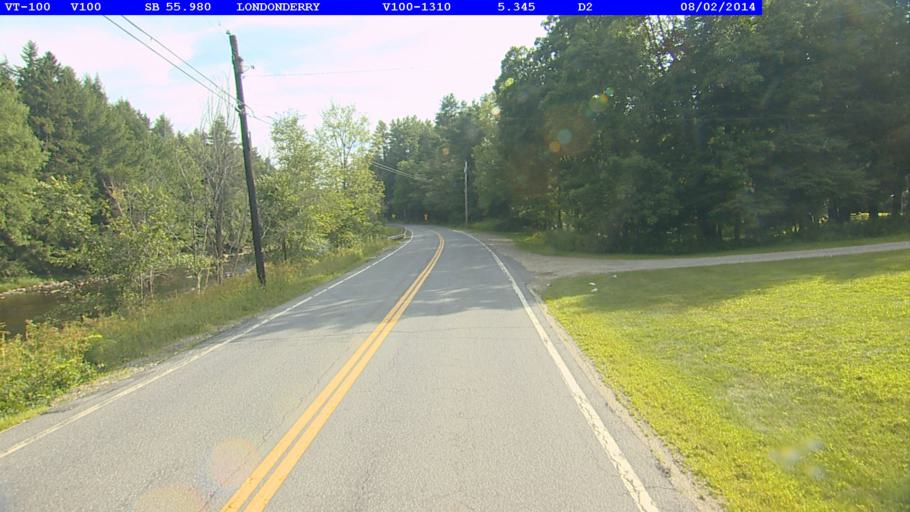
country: US
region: Vermont
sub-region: Windsor County
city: Chester
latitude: 43.2236
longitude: -72.8190
